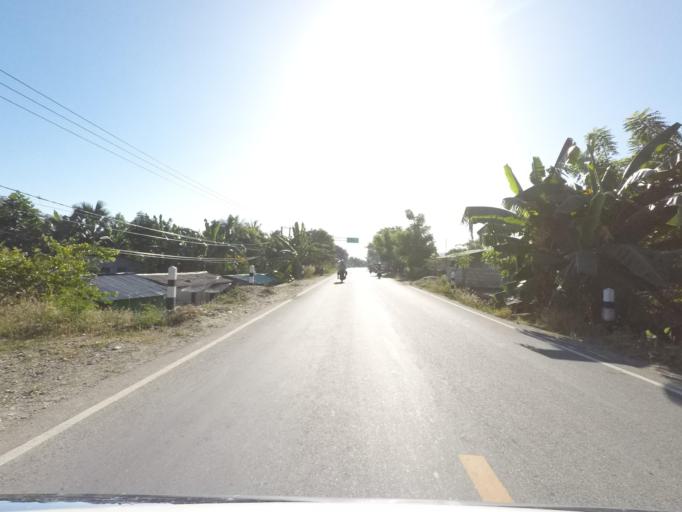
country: ID
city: Metinaro
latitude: -8.5444
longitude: 125.6716
